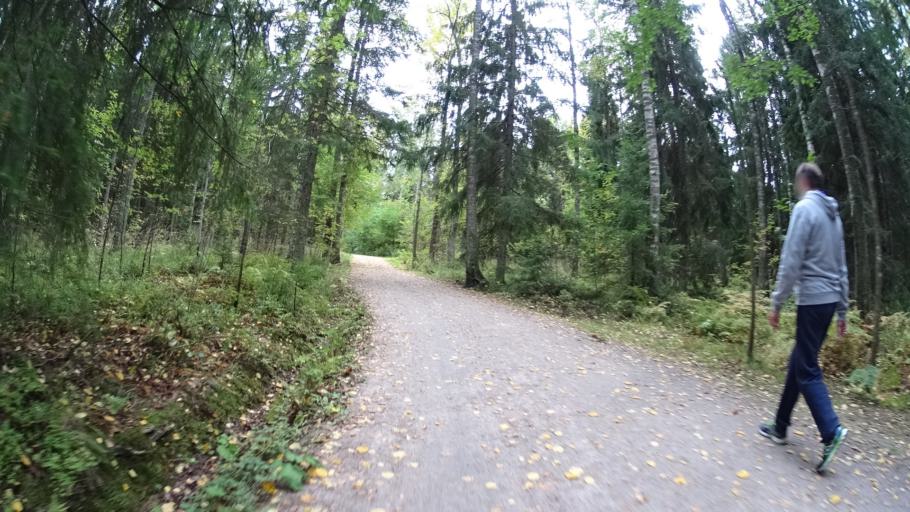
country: FI
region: Uusimaa
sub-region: Helsinki
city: Helsinki
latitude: 60.2516
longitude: 24.9119
